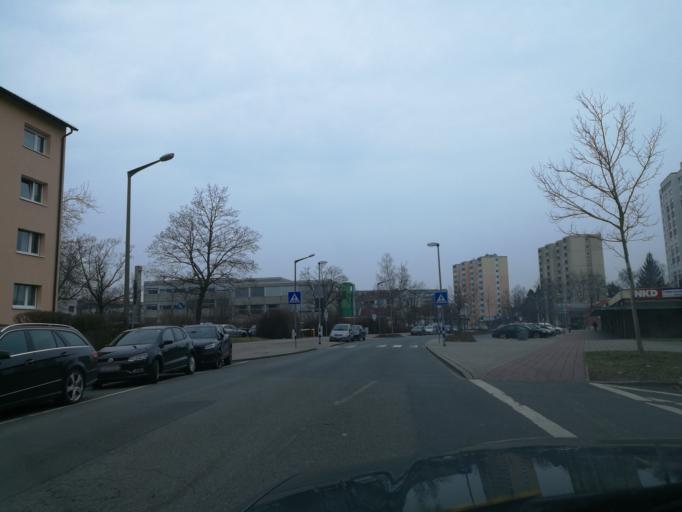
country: DE
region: Bavaria
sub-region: Regierungsbezirk Mittelfranken
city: Furth
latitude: 49.4791
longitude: 10.9565
